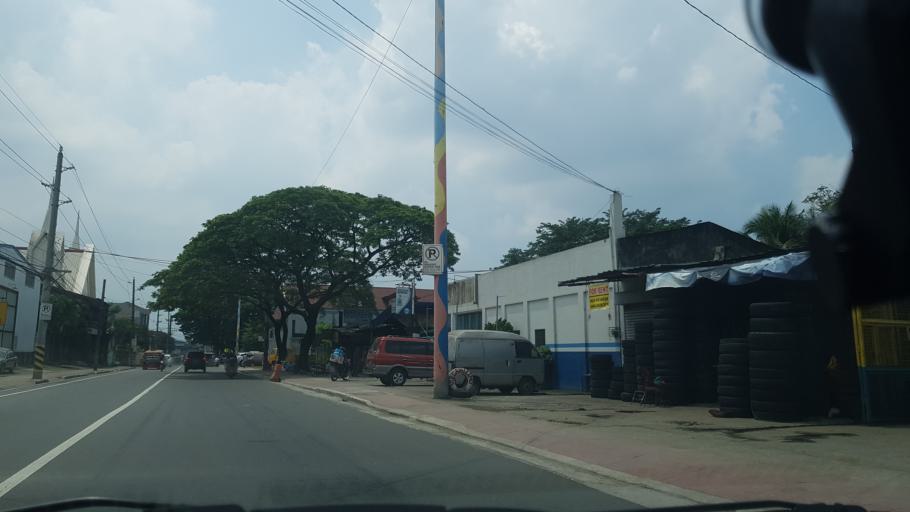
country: PH
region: Calabarzon
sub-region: Province of Rizal
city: Antipolo
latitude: 14.6601
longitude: 121.1049
